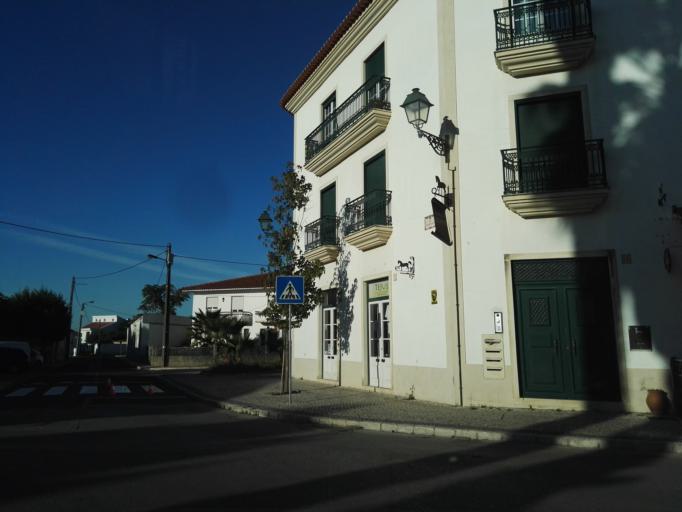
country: PT
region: Santarem
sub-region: Golega
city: Golega
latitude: 39.4028
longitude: -8.4886
